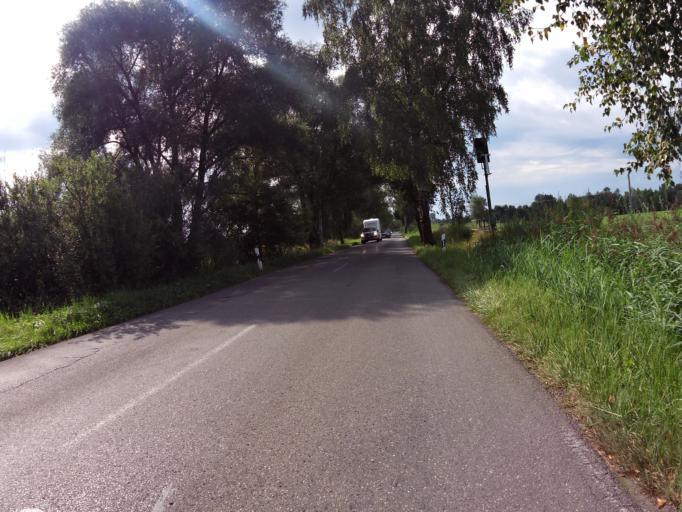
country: DE
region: Bavaria
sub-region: Upper Bavaria
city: Diessen am Ammersee
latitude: 47.9346
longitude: 11.1088
